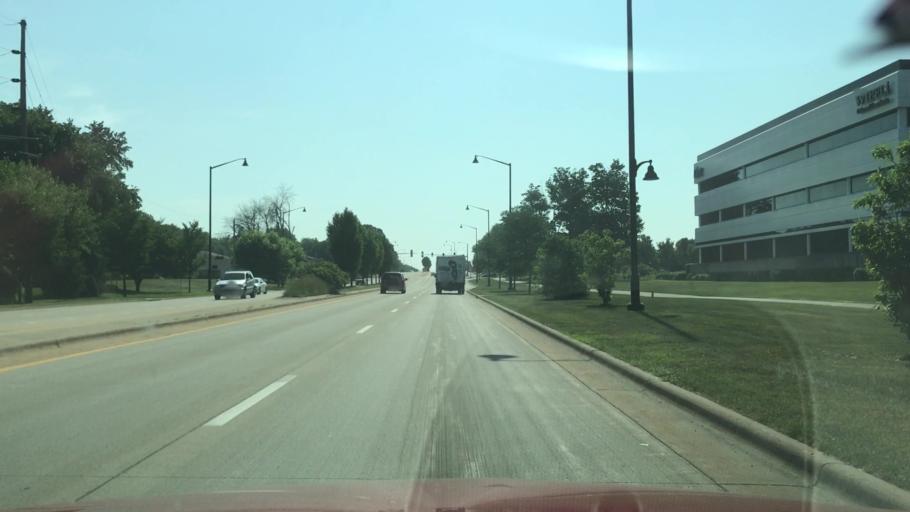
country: US
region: Illinois
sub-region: Winnebago County
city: Cherry Valley
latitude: 42.2382
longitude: -89.0222
